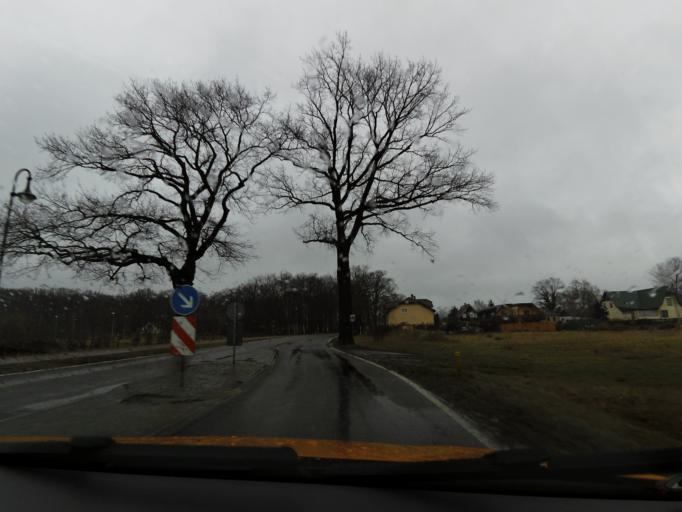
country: DE
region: Brandenburg
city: Rangsdorf
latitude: 52.2675
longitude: 13.4597
